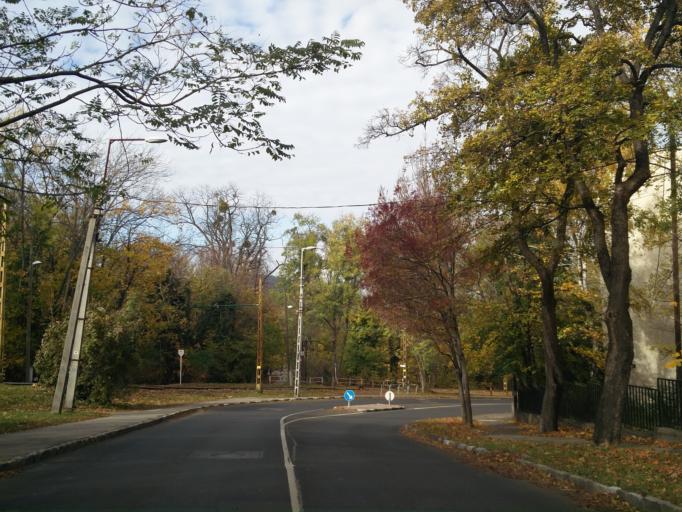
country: HU
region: Budapest
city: Budapest XII. keruelet
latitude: 47.5004
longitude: 18.9895
